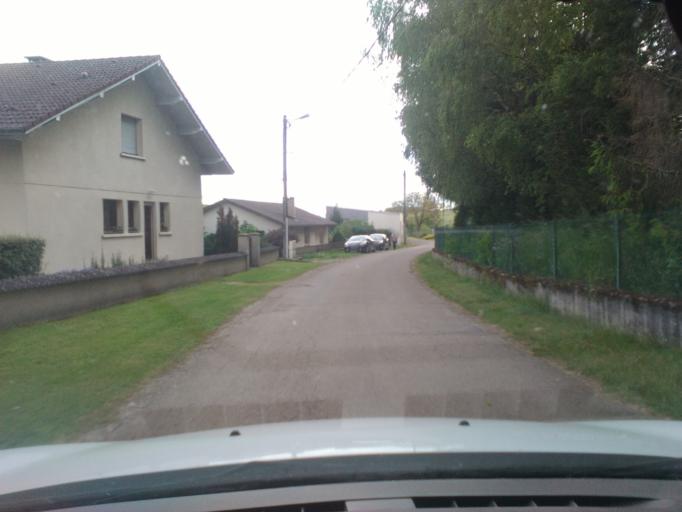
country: FR
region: Lorraine
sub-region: Departement des Vosges
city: Mirecourt
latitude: 48.3492
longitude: 6.1466
